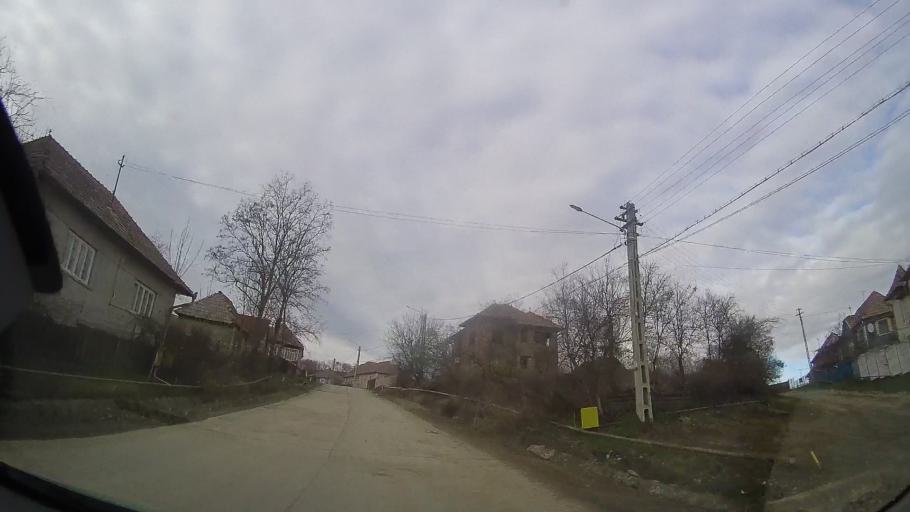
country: RO
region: Bistrita-Nasaud
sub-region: Comuna Sanmihaiu de Campie
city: Sanmihaiu de Campie
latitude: 46.8901
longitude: 24.3338
